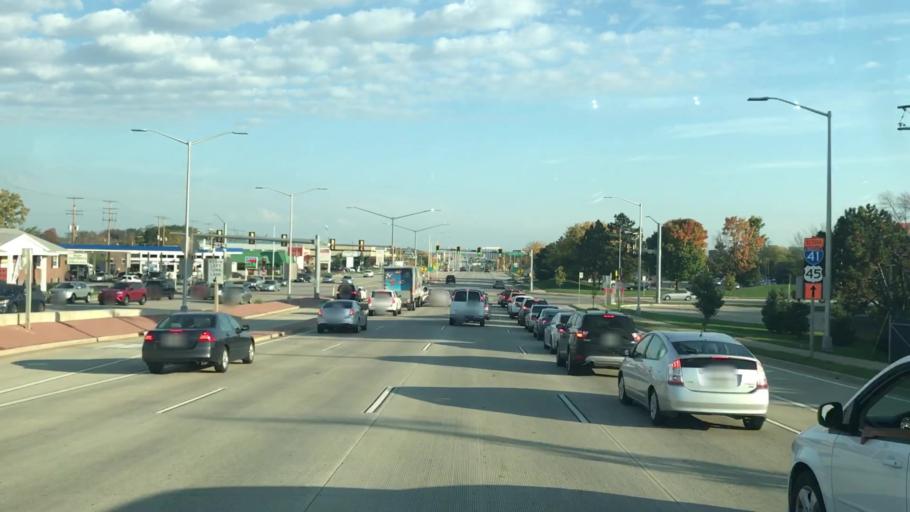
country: US
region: Wisconsin
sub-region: Waukesha County
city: Elm Grove
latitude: 43.0373
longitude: -88.0470
